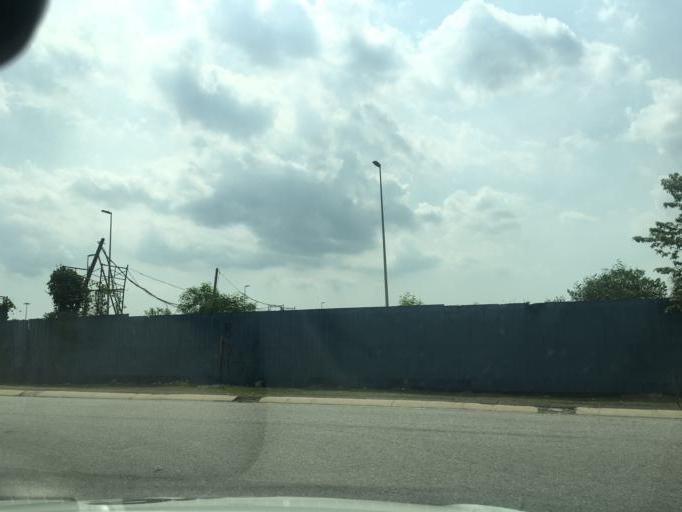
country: MY
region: Selangor
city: Shah Alam
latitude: 3.0819
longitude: 101.4790
